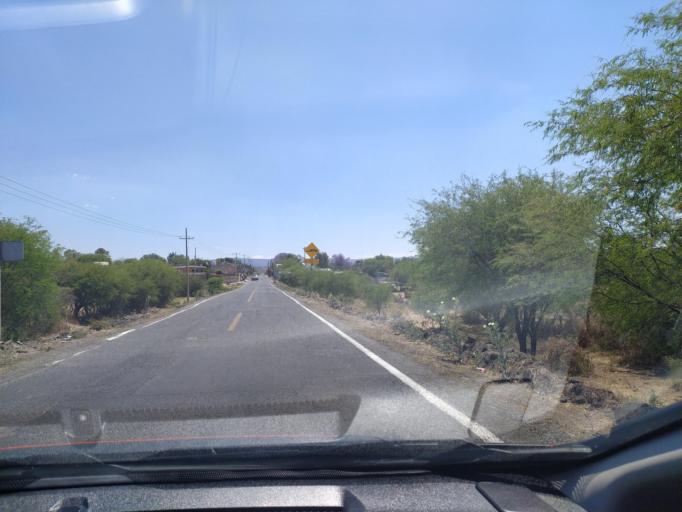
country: MX
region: Guanajuato
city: Ciudad Manuel Doblado
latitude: 20.7532
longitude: -101.8257
